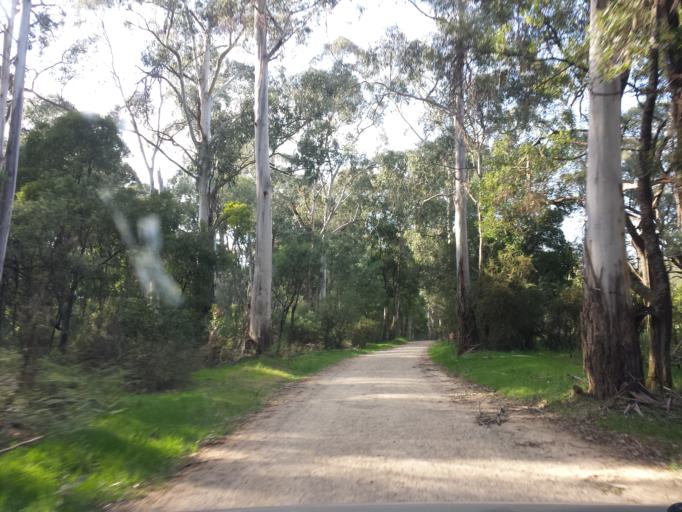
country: AU
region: Victoria
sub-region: Murrindindi
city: Alexandra
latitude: -37.3404
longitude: 145.7465
